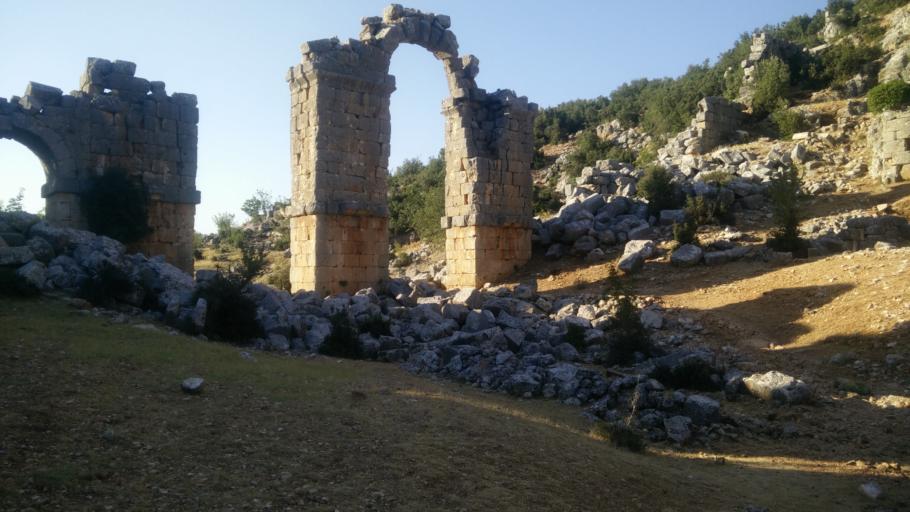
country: TR
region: Mersin
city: Kirobasi
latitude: 36.5858
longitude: 33.9691
